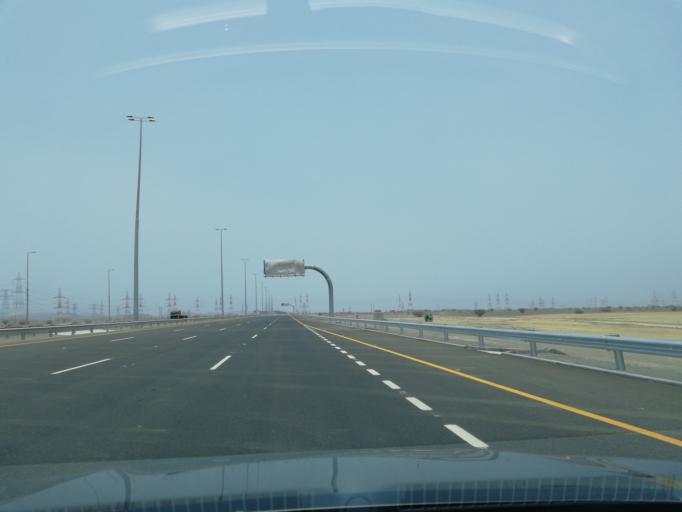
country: OM
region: Al Batinah
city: Al Liwa'
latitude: 24.4121
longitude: 56.5372
